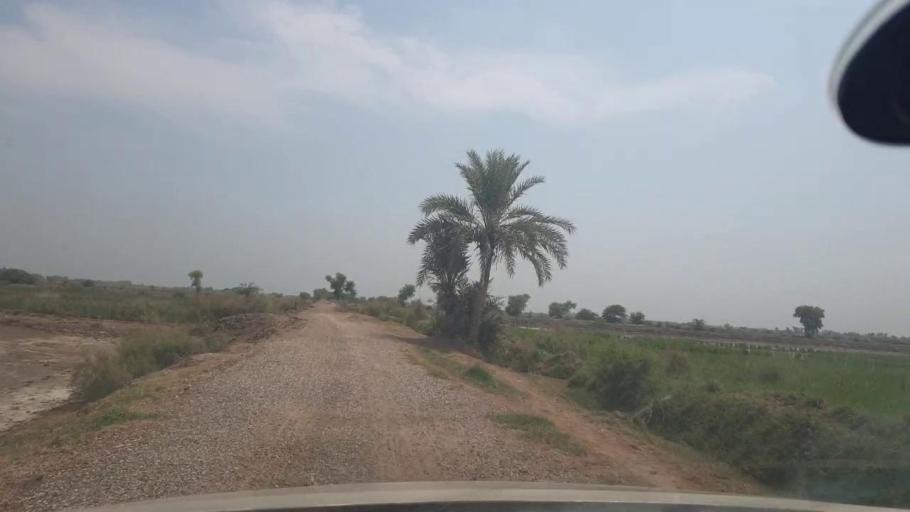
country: PK
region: Sindh
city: Jacobabad
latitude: 28.2278
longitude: 68.3967
